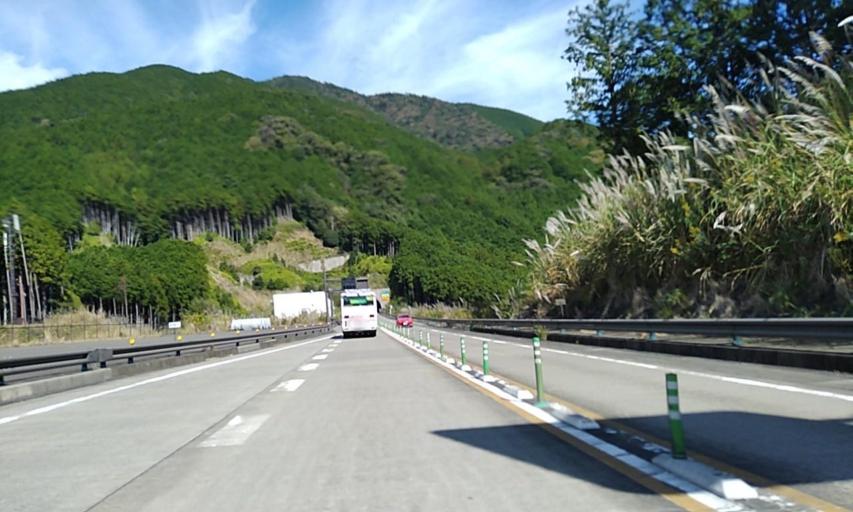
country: JP
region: Mie
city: Owase
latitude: 33.9737
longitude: 136.1650
